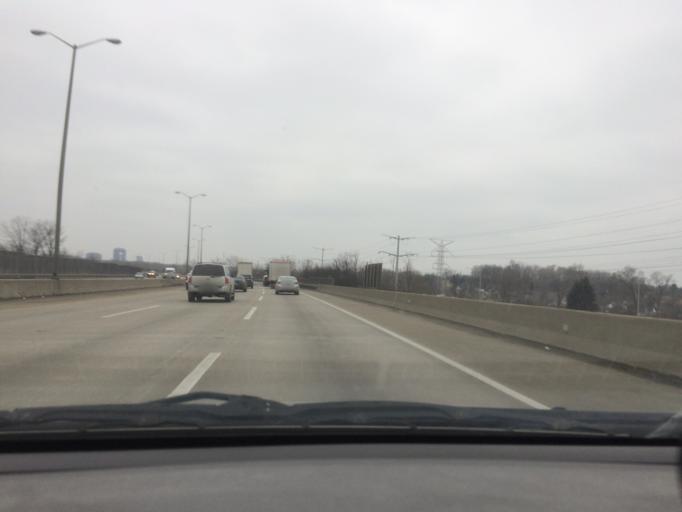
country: US
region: Illinois
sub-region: DuPage County
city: Glen Ellyn
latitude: 41.8599
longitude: -88.0417
